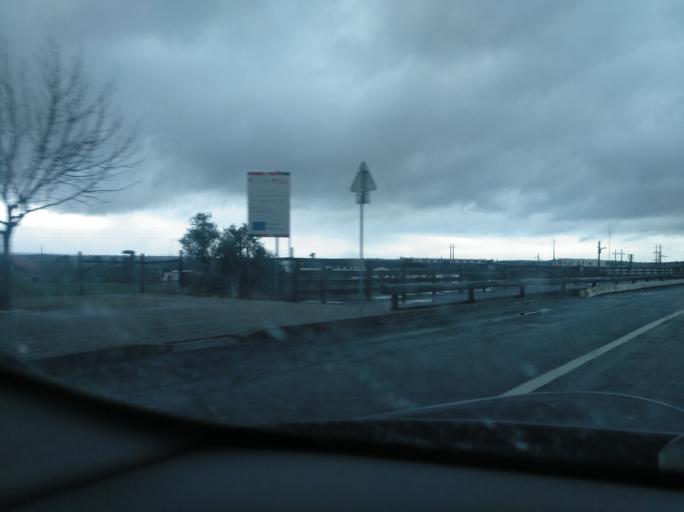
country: PT
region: Beja
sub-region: Aljustrel
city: Aljustrel
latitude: 37.8787
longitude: -8.1549
